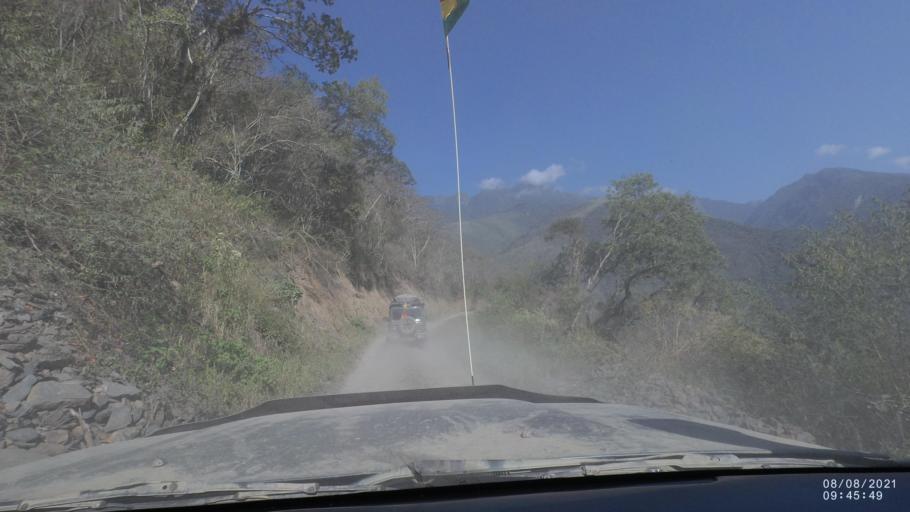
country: BO
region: La Paz
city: Quime
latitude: -16.6049
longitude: -66.7277
